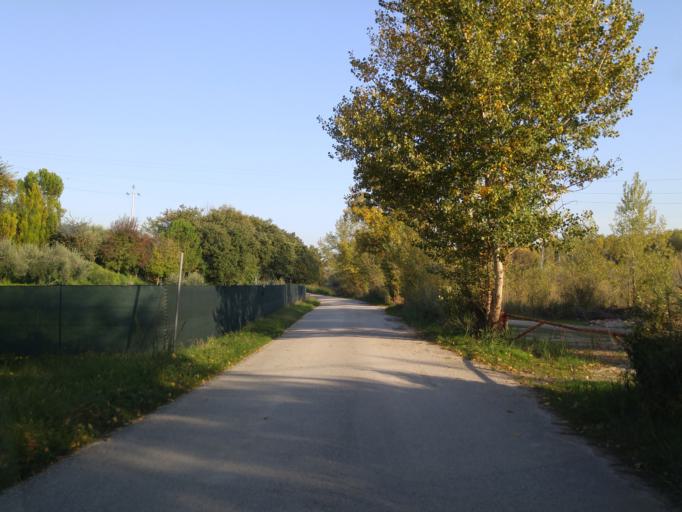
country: IT
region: The Marches
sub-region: Provincia di Pesaro e Urbino
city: Montefelcino
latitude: 43.7122
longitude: 12.8535
